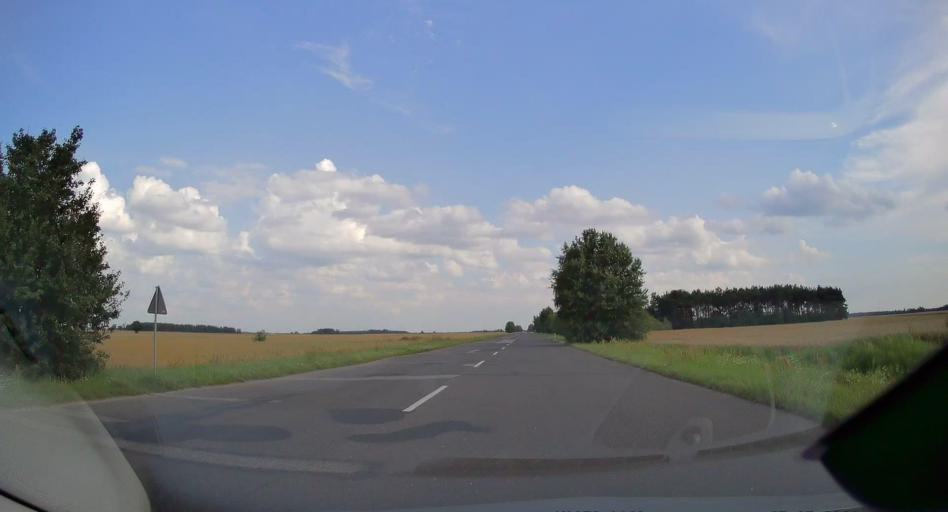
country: PL
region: Lodz Voivodeship
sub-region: Powiat tomaszowski
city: Rzeczyca
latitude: 51.6626
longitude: 20.2683
